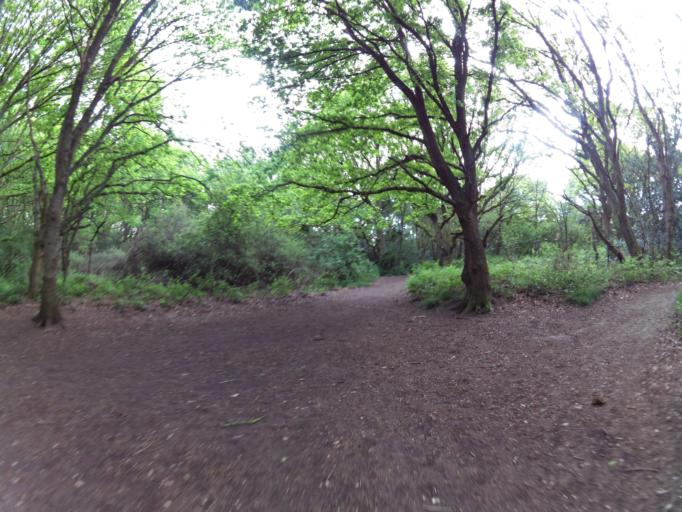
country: GB
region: England
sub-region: Suffolk
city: Kesgrave
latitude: 52.0575
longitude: 1.2142
